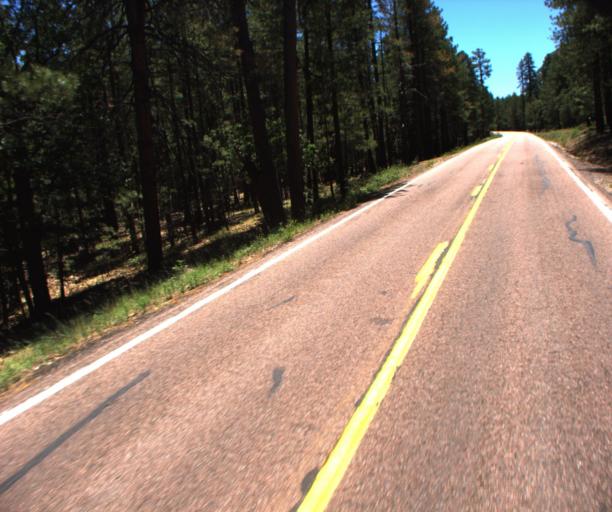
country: US
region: Arizona
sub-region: Gila County
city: Pine
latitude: 34.5191
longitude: -111.3423
